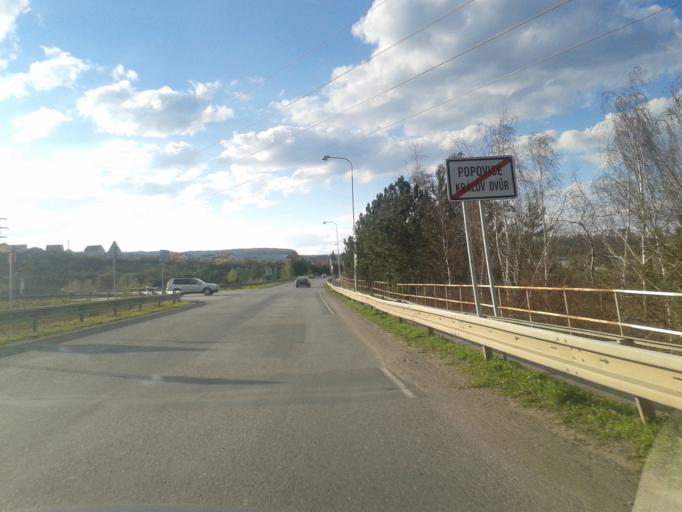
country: CZ
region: Central Bohemia
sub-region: Okres Beroun
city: Kraluv Dvur
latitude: 49.9343
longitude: 14.0228
